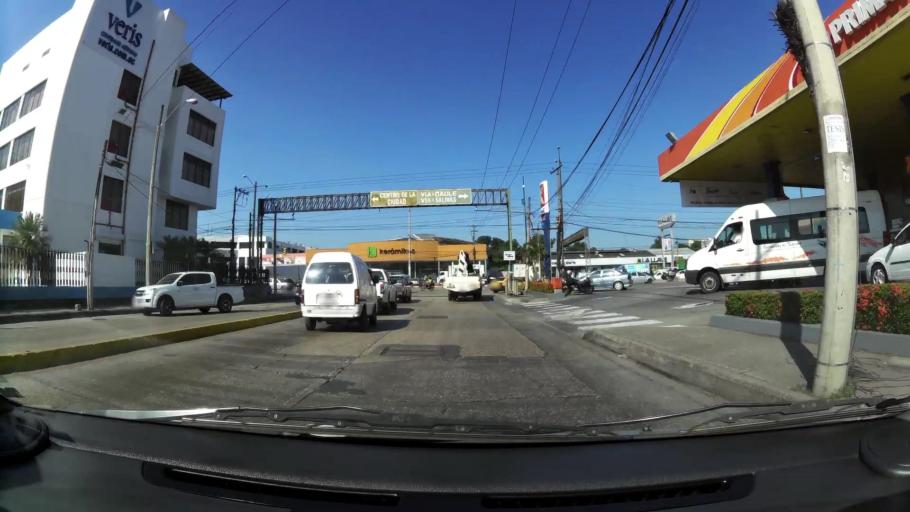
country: EC
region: Guayas
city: Eloy Alfaro
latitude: -2.1491
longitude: -79.9009
